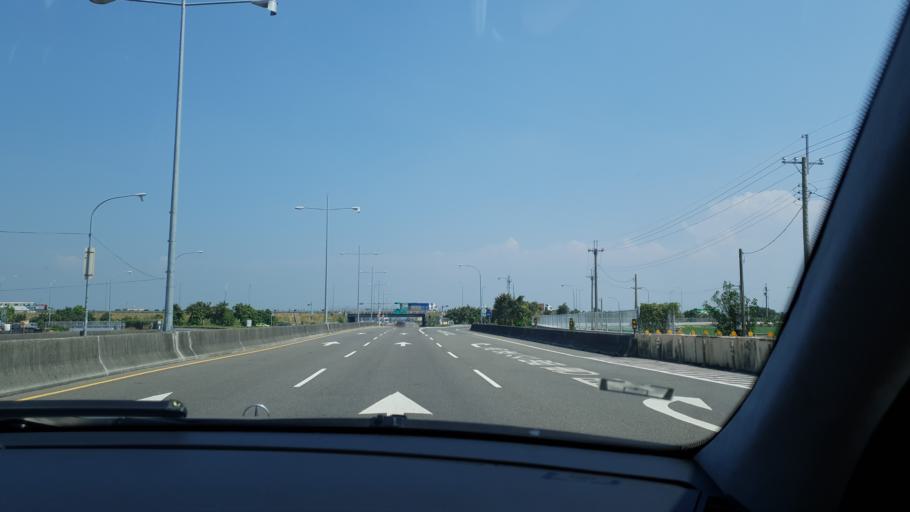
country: TW
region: Taiwan
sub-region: Yunlin
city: Douliu
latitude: 23.7358
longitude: 120.4676
